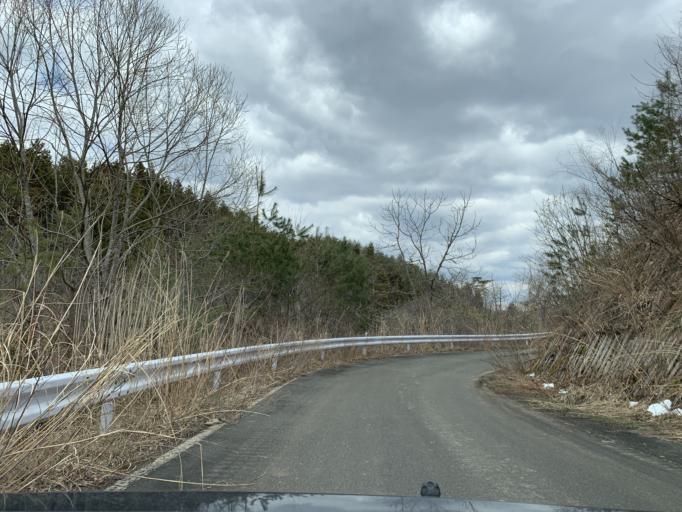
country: JP
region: Iwate
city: Ichinoseki
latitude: 38.9547
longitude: 141.0660
